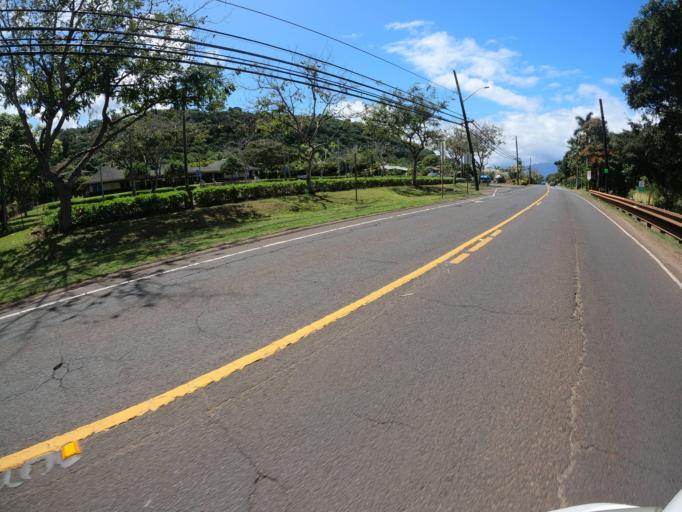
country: US
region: Hawaii
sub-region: Honolulu County
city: Pupukea
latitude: 21.6576
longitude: -158.0581
